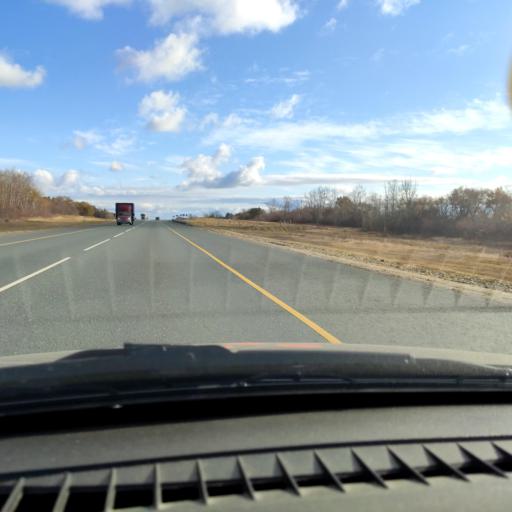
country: RU
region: Samara
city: Balasheyka
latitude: 53.1936
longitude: 48.2359
